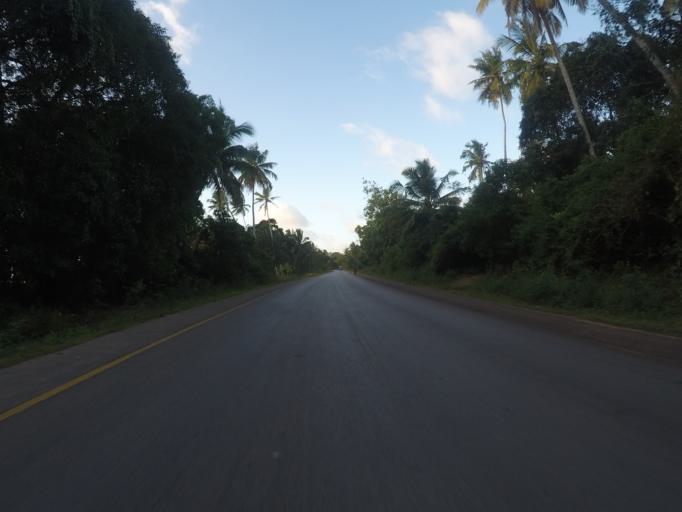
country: TZ
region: Zanzibar Central/South
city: Koani
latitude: -6.1746
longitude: 39.3295
